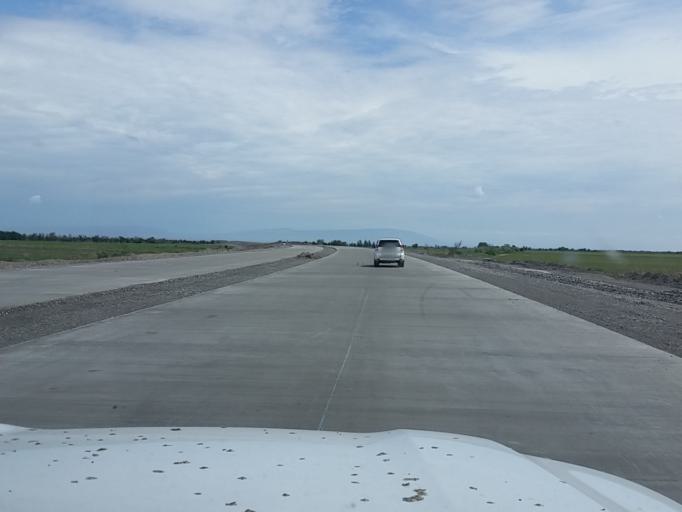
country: KZ
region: Almaty Oblysy
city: Turgen'
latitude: 43.6245
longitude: 78.3703
